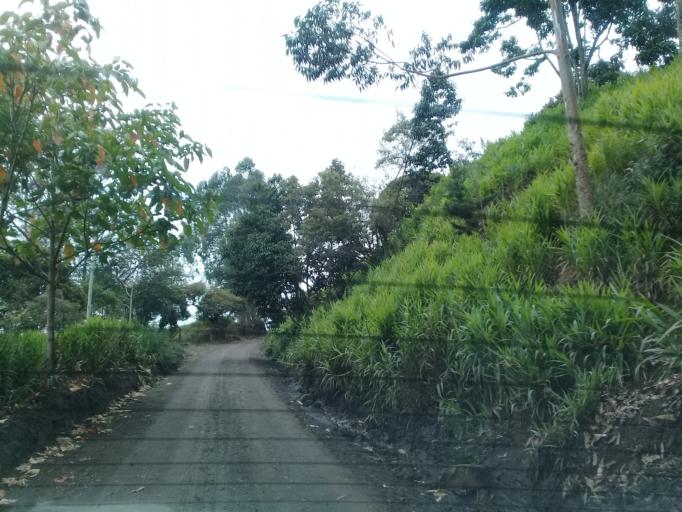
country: CO
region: Cundinamarca
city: Une
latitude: 4.4005
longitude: -73.9866
